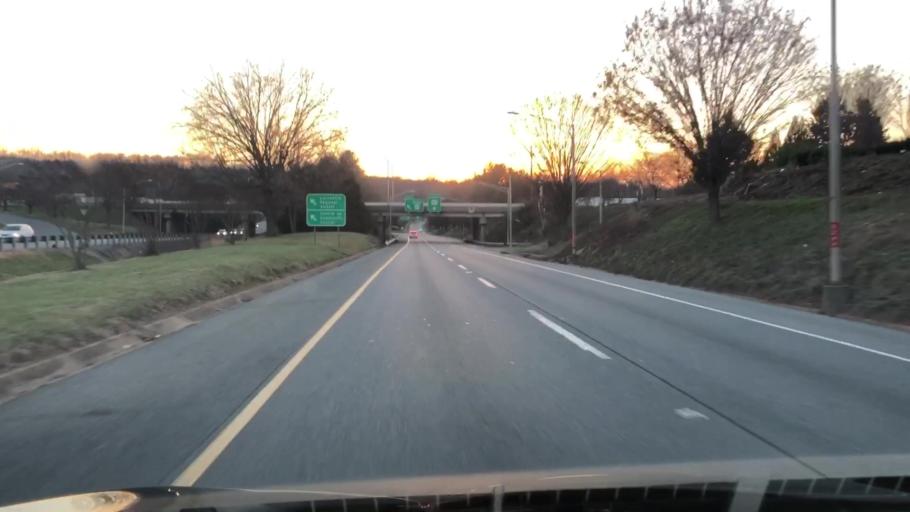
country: US
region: Virginia
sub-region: City of Lynchburg
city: West Lynchburg
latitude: 37.3667
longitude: -79.1810
